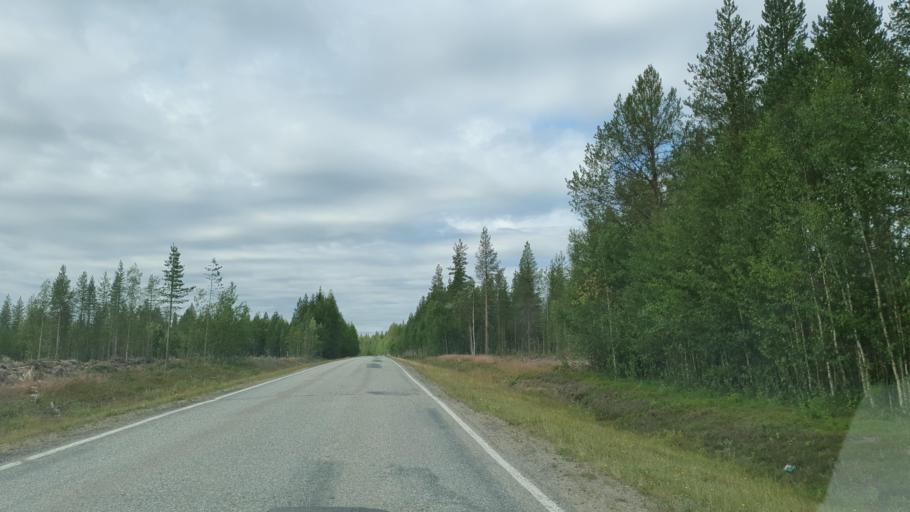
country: FI
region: Lapland
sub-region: Tunturi-Lappi
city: Kittilae
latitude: 67.6159
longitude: 25.3455
